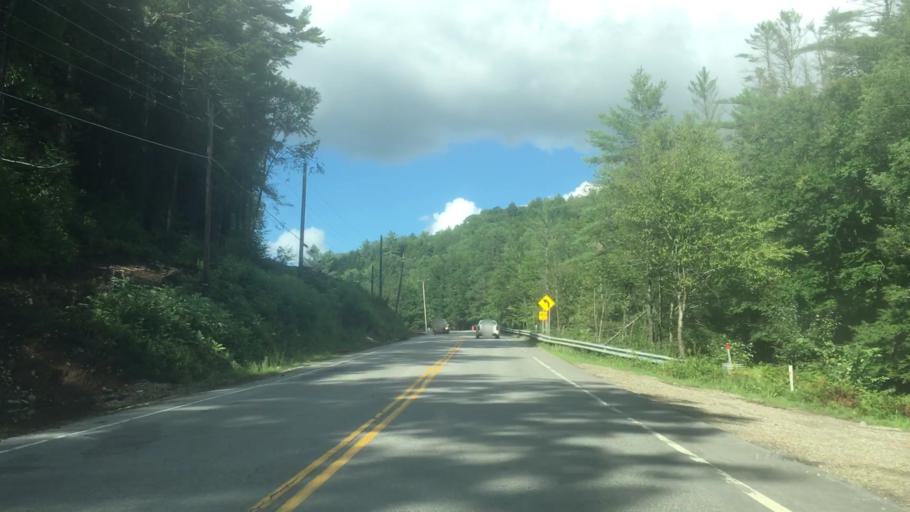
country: US
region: New Hampshire
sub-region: Cheshire County
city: Marlborough
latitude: 42.9863
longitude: -72.2000
